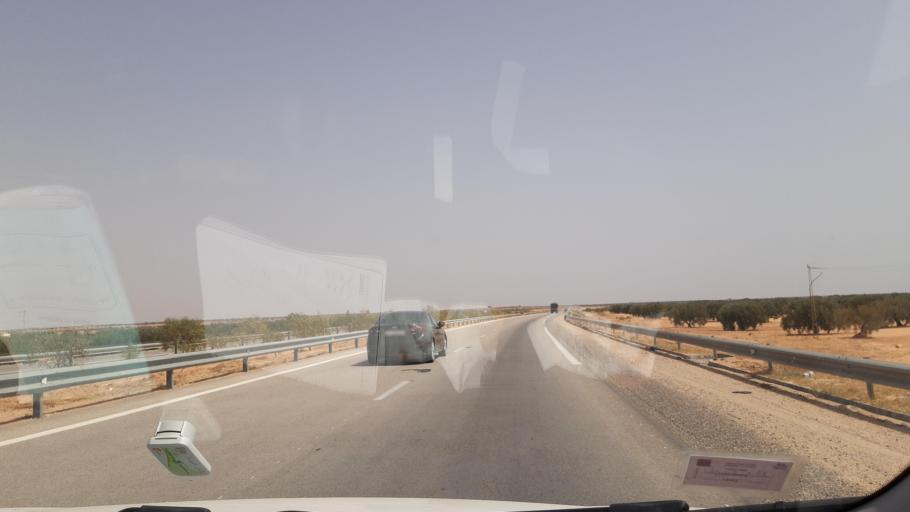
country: TN
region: Safaqis
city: Bi'r `Ali Bin Khalifah
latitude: 34.5260
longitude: 10.1327
